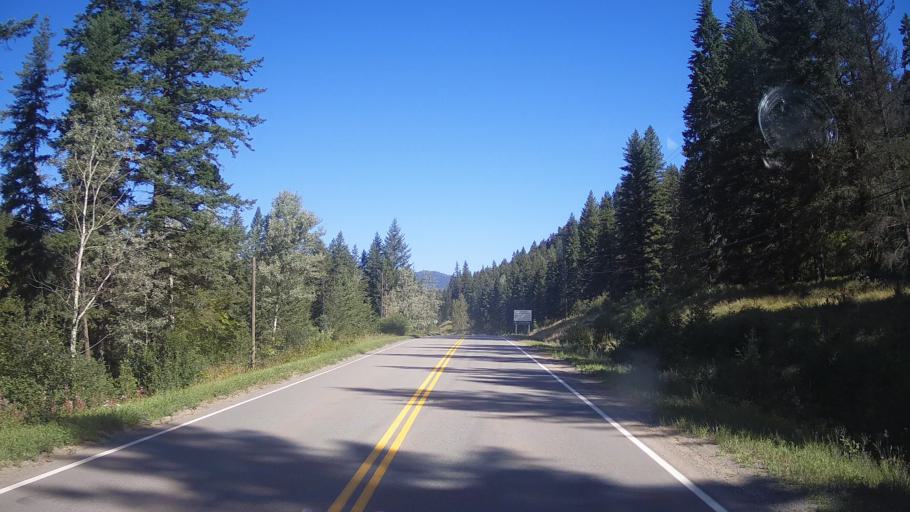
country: CA
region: British Columbia
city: Kamloops
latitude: 51.4484
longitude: -120.2130
